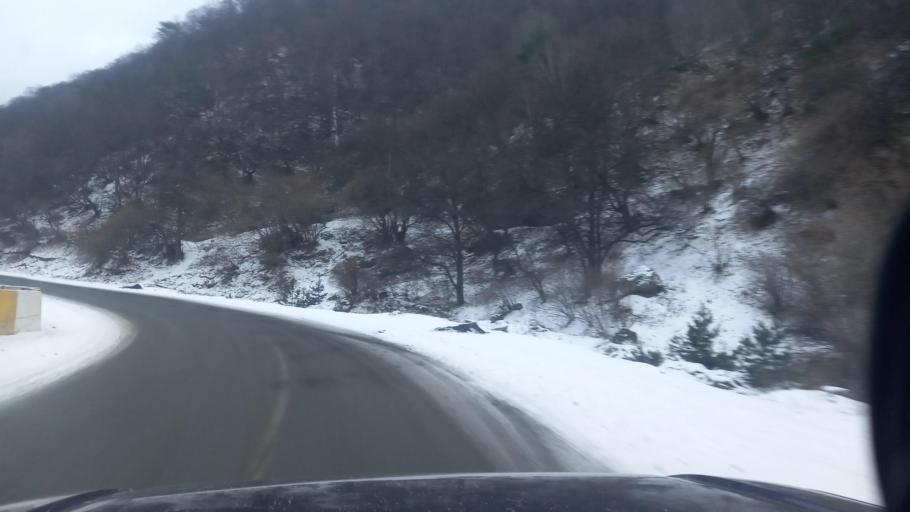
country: RU
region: Ingushetiya
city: Dzhayrakh
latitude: 42.7934
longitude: 44.7629
